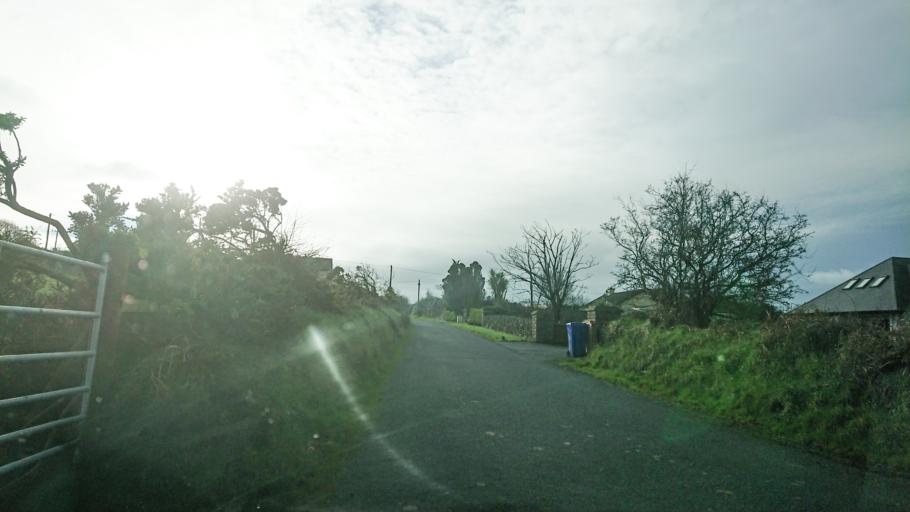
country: IE
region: Munster
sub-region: Waterford
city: Tra Mhor
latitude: 52.1567
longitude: -7.1903
